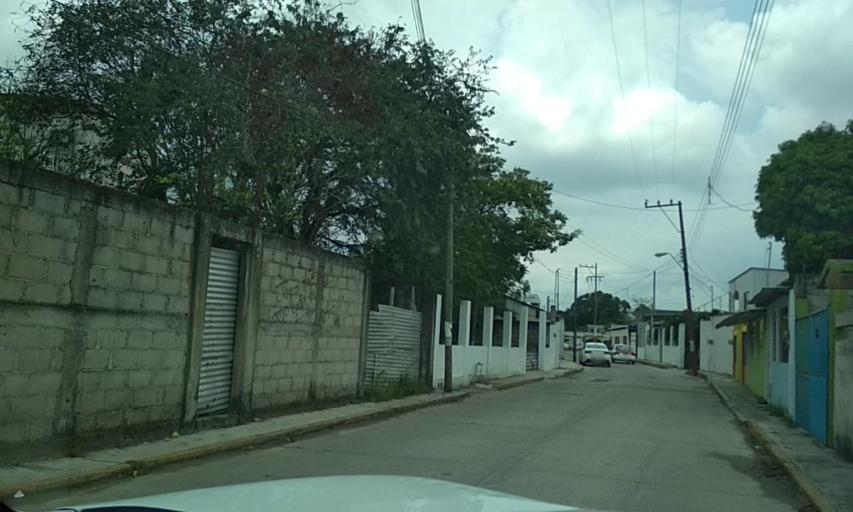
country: MX
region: Veracruz
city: Las Choapas
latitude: 17.8985
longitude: -94.0986
